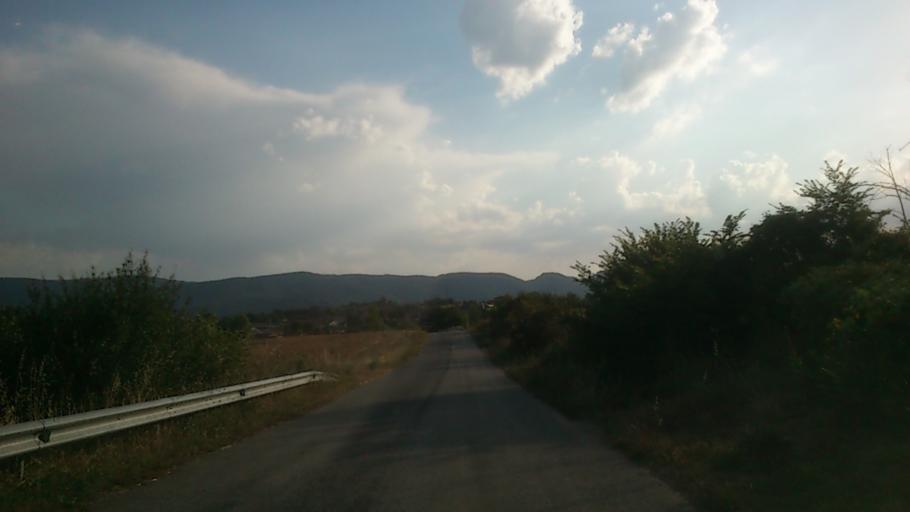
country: ES
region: Castille and Leon
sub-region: Provincia de Burgos
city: Frias
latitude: 42.7980
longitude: -3.2644
